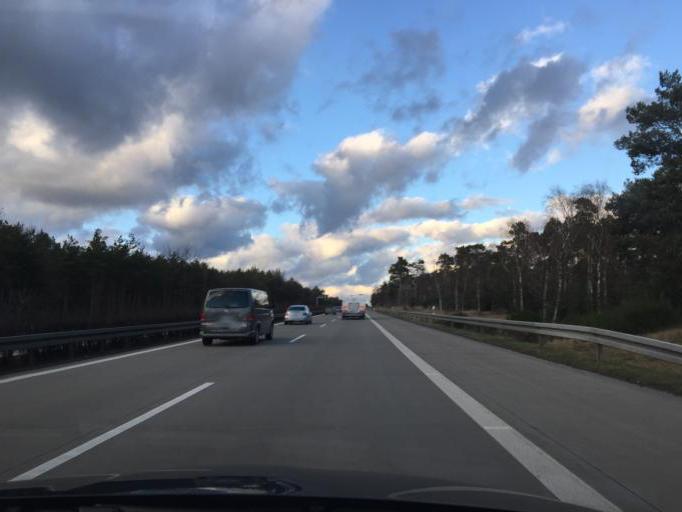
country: DE
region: Brandenburg
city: Teupitz
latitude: 52.0722
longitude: 13.6509
